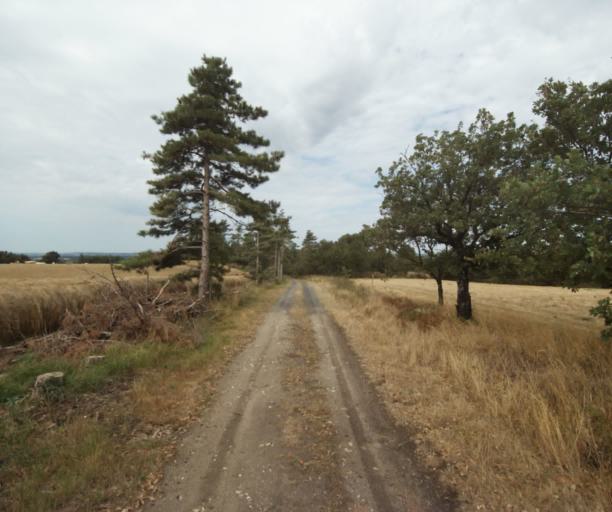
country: FR
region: Midi-Pyrenees
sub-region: Departement de la Haute-Garonne
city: Revel
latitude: 43.4401
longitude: 1.9846
